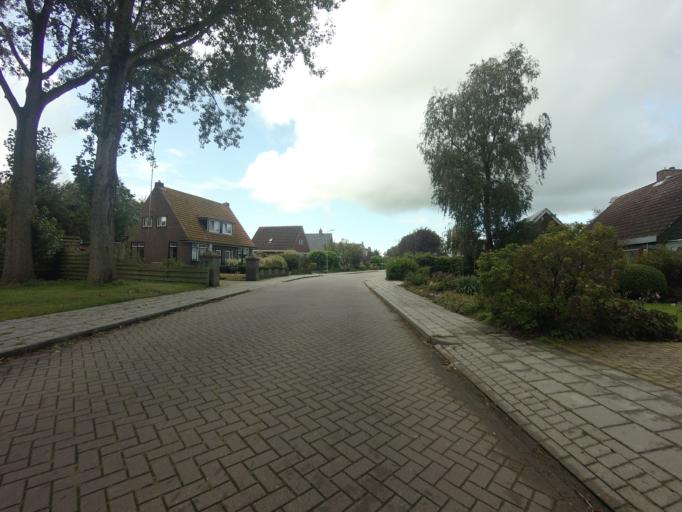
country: NL
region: Friesland
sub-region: Gemeente Boarnsterhim
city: Warten
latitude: 53.1513
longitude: 5.9040
